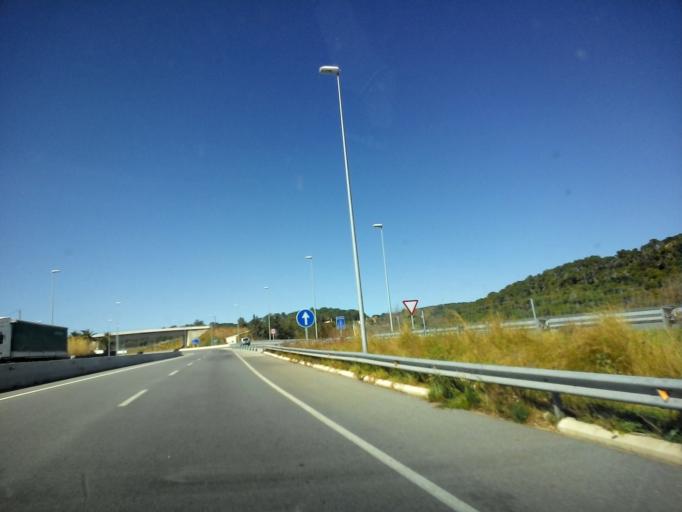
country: ES
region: Catalonia
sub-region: Provincia de Girona
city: Palamos
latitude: 41.8587
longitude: 3.1179
